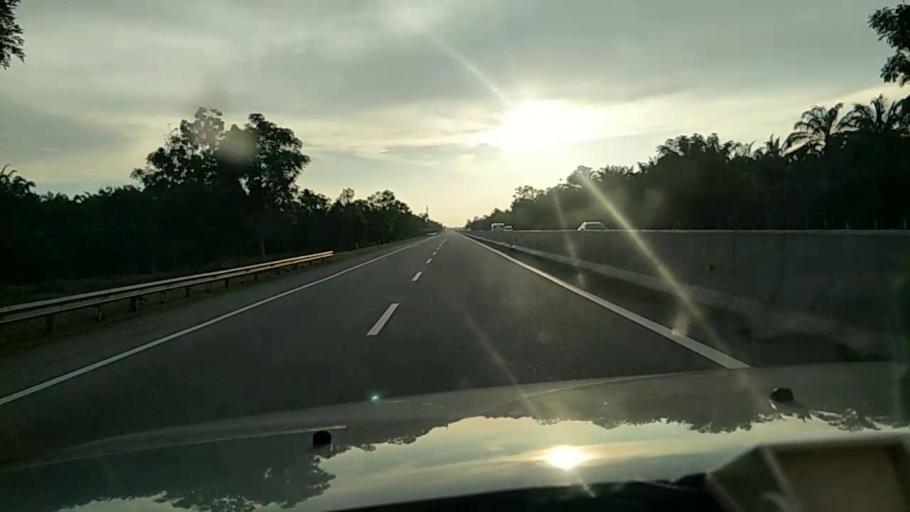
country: MY
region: Selangor
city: Batu Arang
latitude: 3.2879
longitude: 101.4163
